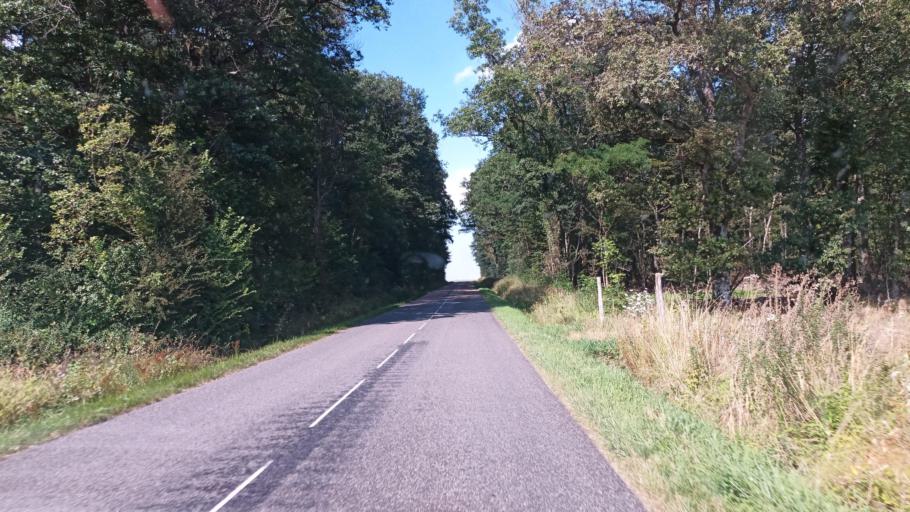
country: FR
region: Bourgogne
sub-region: Departement de l'Yonne
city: Saint-Valerien
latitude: 48.1586
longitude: 3.0982
